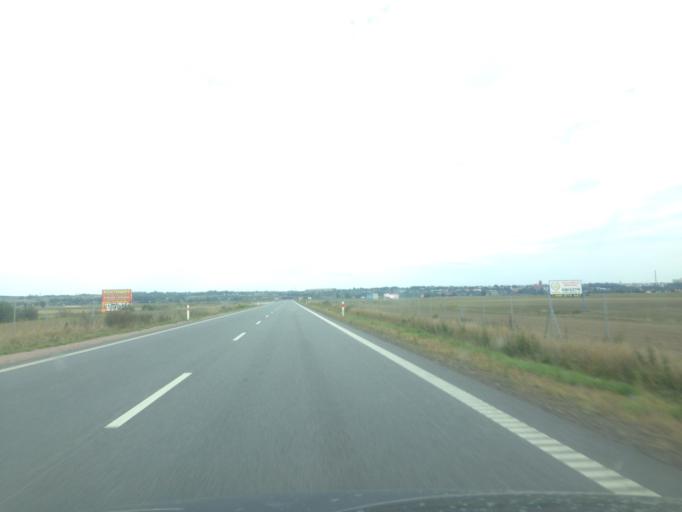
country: PL
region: Pomeranian Voivodeship
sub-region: Powiat kwidzynski
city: Kwidzyn
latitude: 53.7590
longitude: 18.8809
